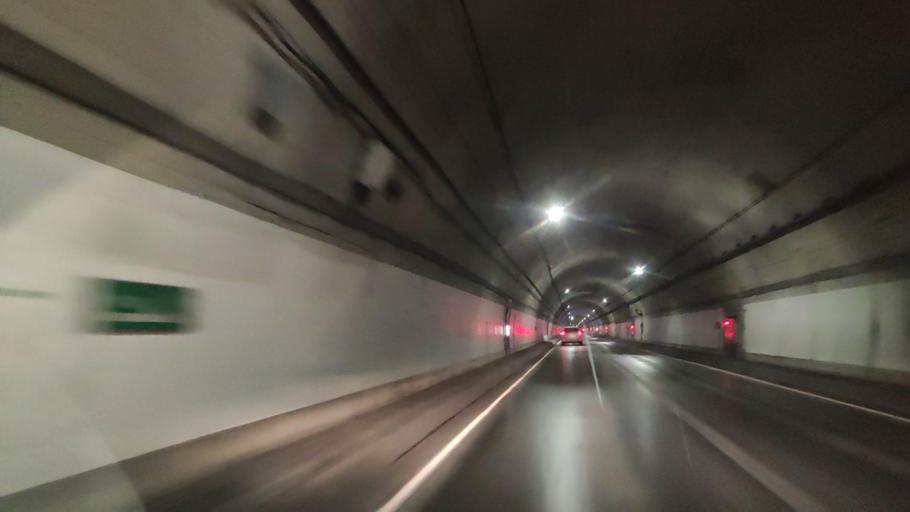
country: JP
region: Hokkaido
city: Rumoi
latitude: 43.7069
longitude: 141.3343
